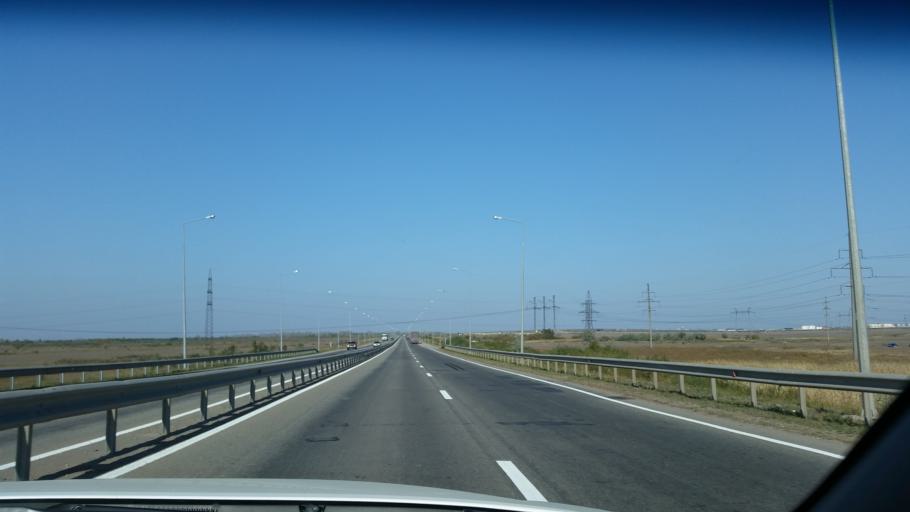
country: KZ
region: Astana Qalasy
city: Astana
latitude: 51.2338
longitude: 71.3295
